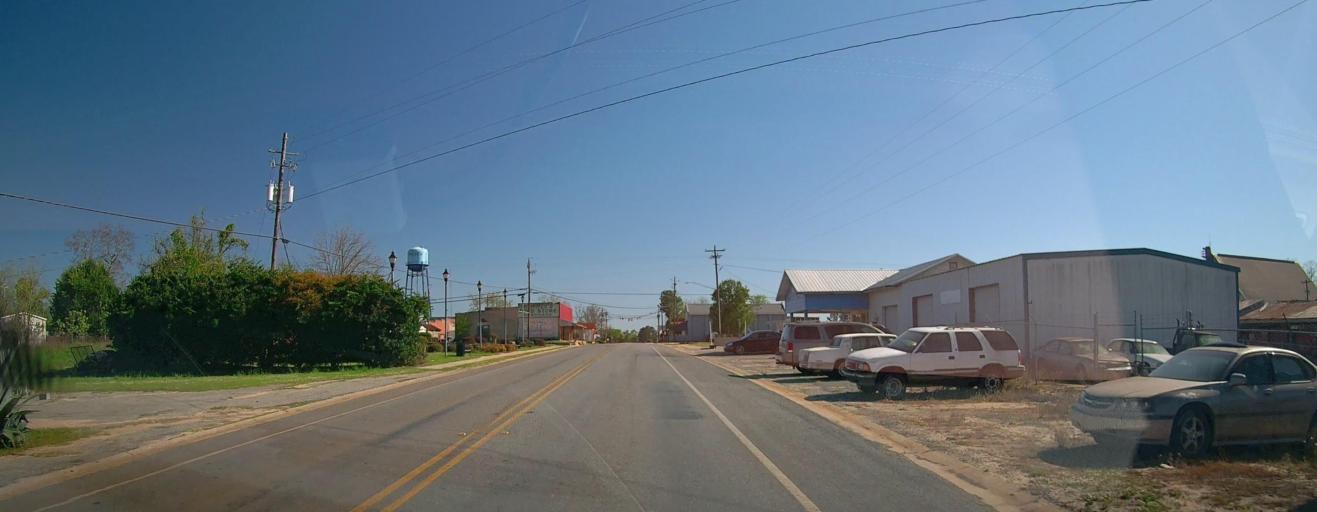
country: US
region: Georgia
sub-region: Wilcox County
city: Rochelle
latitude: 32.1118
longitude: -83.5011
